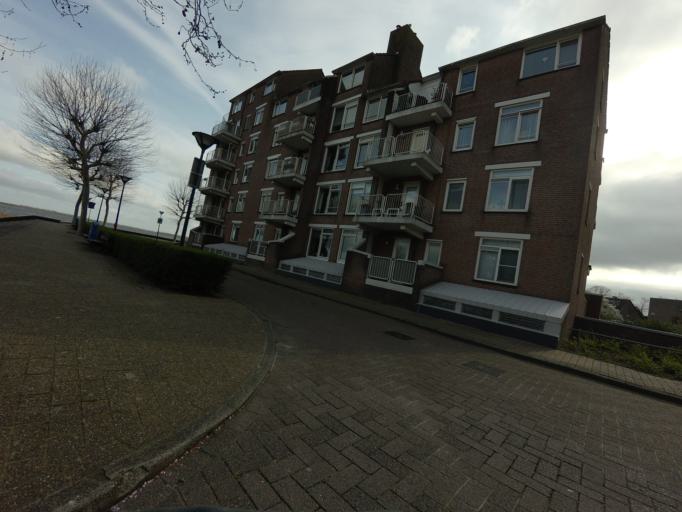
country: NL
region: North Holland
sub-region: Gemeente Huizen
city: Huizen
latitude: 52.3053
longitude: 5.2593
